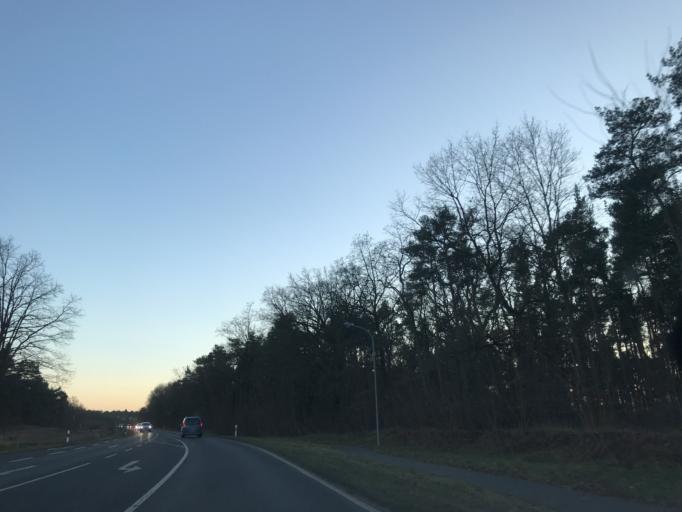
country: DE
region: Brandenburg
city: Premnitz
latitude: 52.5541
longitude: 12.3276
